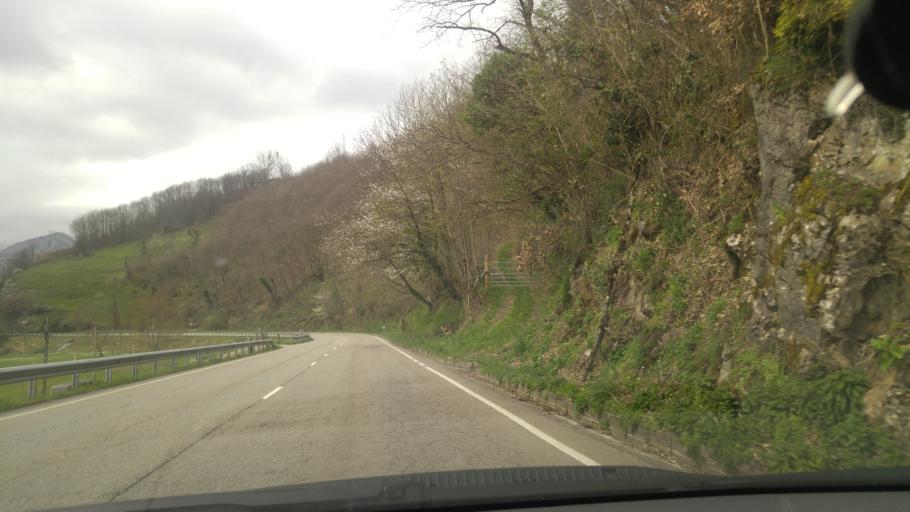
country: ES
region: Asturias
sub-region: Province of Asturias
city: Rio Aller
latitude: 43.1294
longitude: -5.5659
